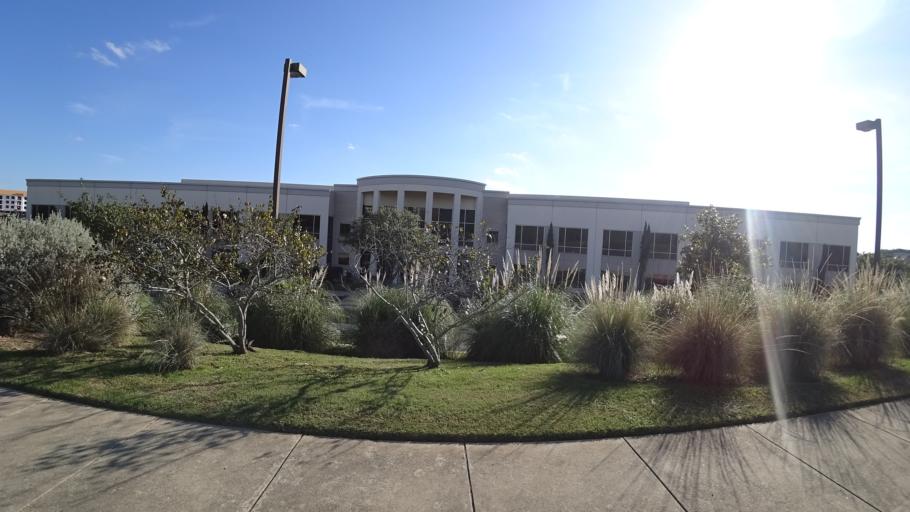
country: US
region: Texas
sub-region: Travis County
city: Barton Creek
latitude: 30.2496
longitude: -97.8649
